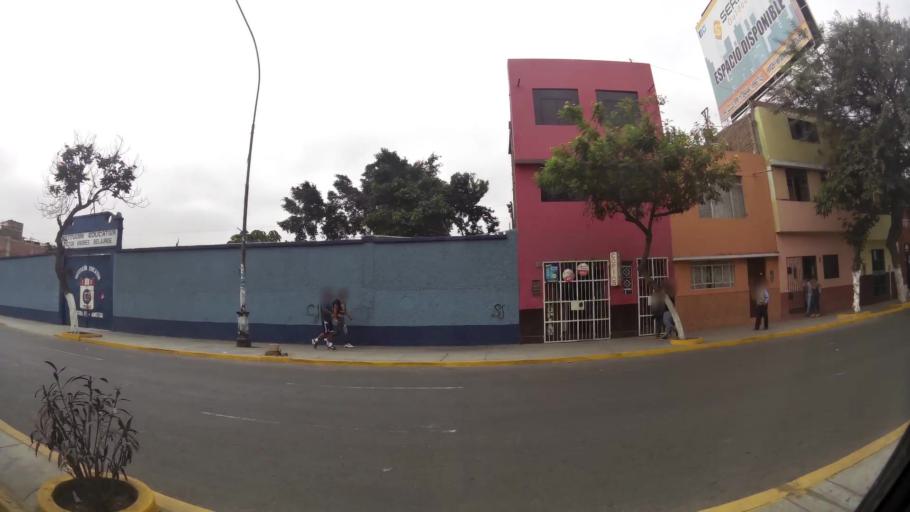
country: PE
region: La Libertad
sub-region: Provincia de Trujillo
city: Trujillo
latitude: -8.1063
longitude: -79.0233
